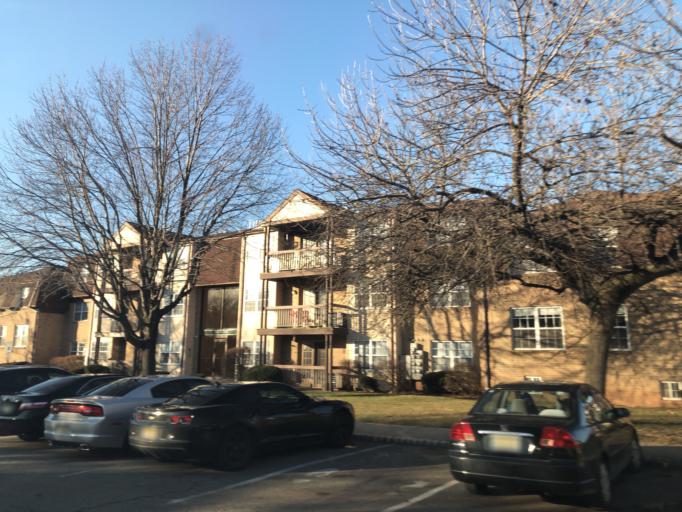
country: US
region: New Jersey
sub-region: Middlesex County
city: Woodbridge
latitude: 40.5490
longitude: -74.2989
